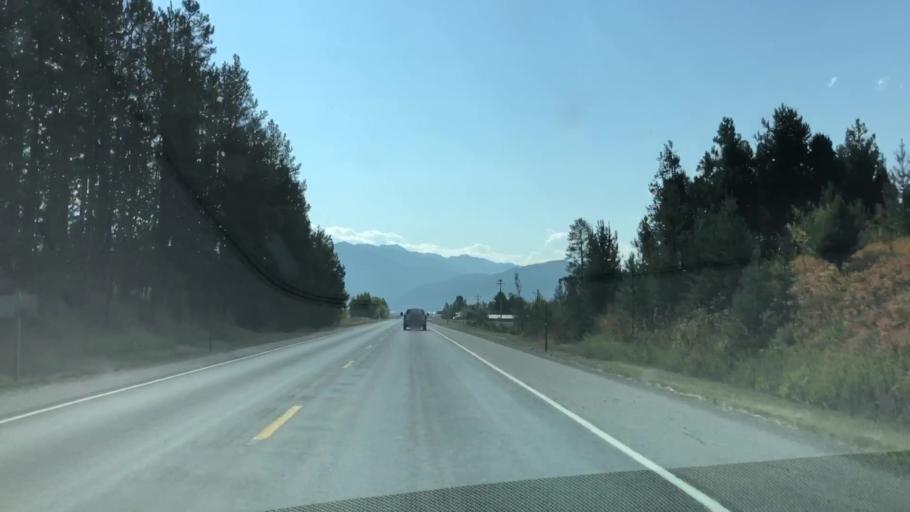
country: US
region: Wyoming
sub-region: Teton County
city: Hoback
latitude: 43.1964
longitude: -111.0403
